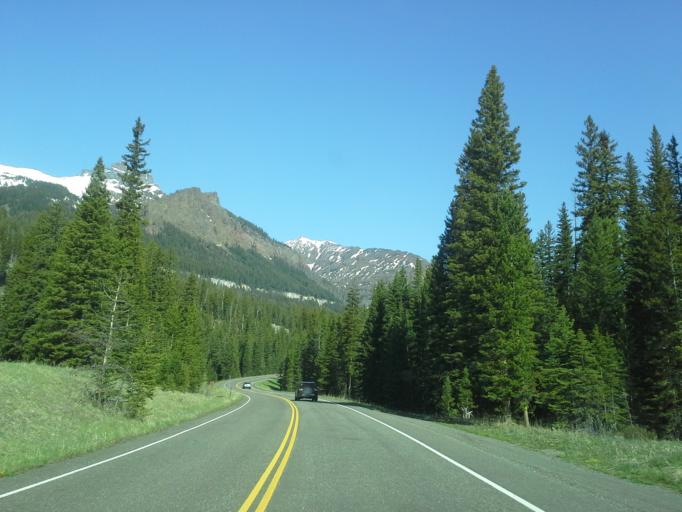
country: US
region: Montana
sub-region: Carbon County
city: Red Lodge
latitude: 44.9754
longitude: -109.8353
